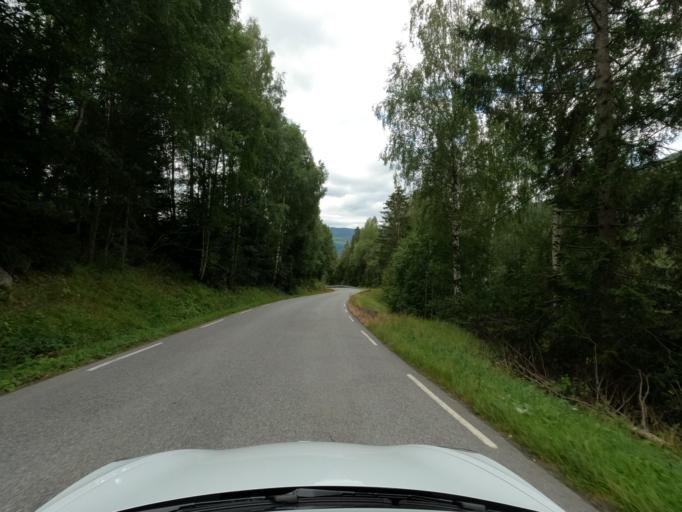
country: NO
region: Telemark
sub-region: Tinn
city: Rjukan
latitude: 60.0066
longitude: 8.8347
